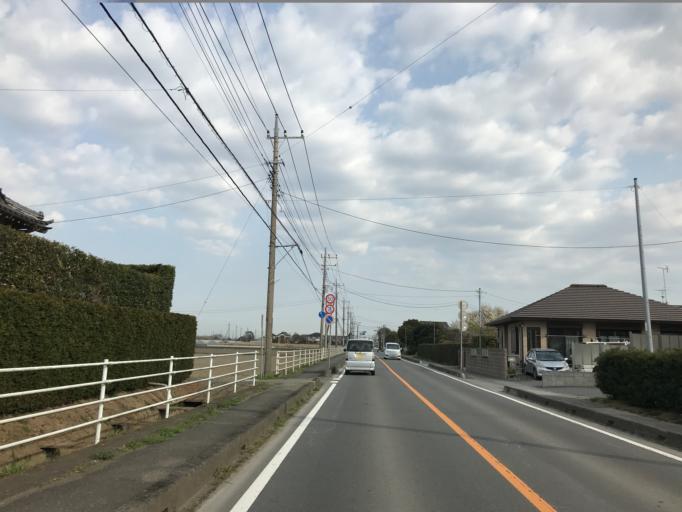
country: JP
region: Ibaraki
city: Mitsukaido
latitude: 35.9941
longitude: 140.0168
